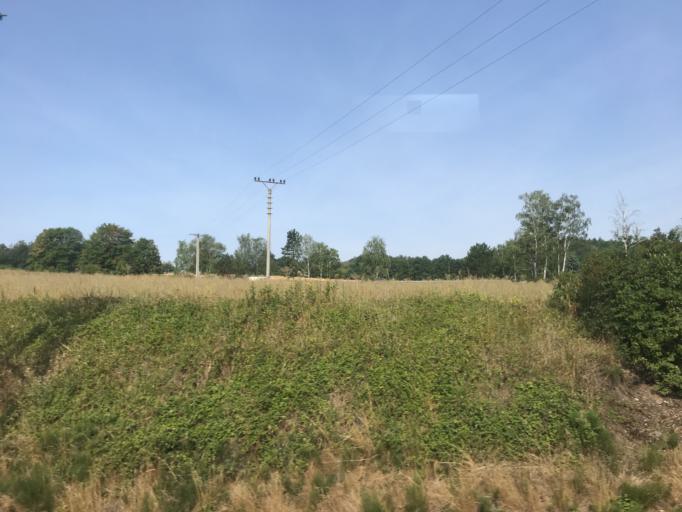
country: CZ
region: Central Bohemia
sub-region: Okres Benesov
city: Cercany
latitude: 49.8588
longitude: 14.6957
